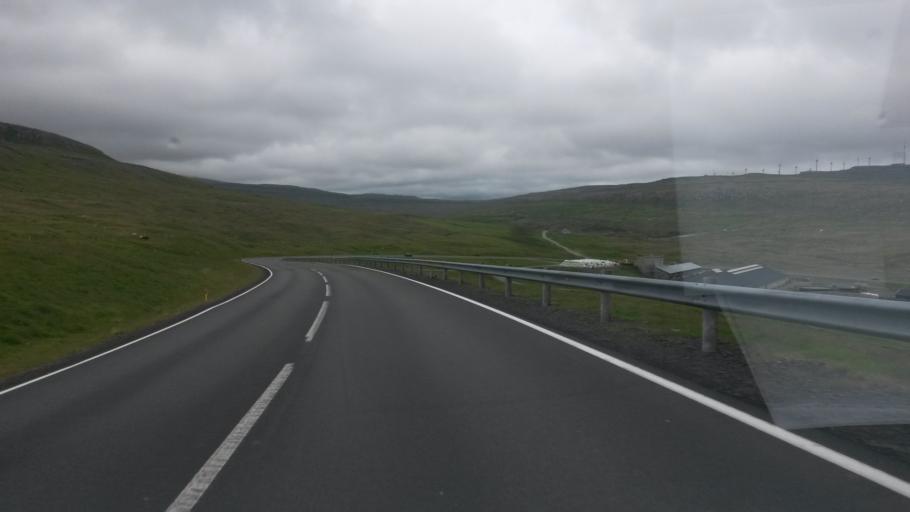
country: FO
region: Streymoy
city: Hoyvik
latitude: 61.9979
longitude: -6.8442
